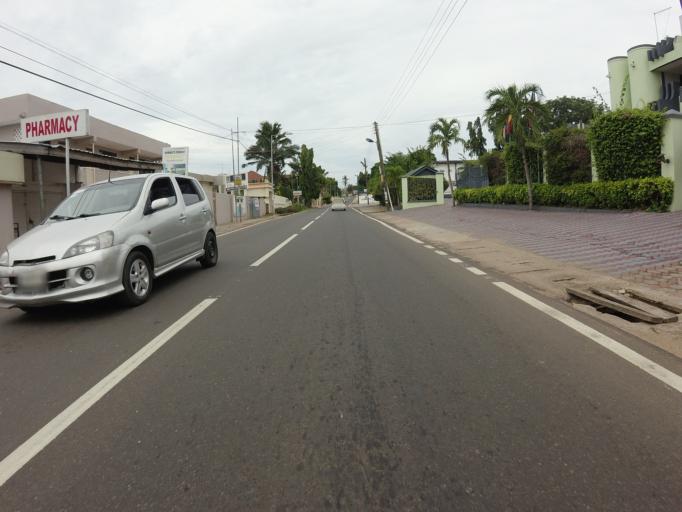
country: GH
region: Greater Accra
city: Dome
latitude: 5.6011
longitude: -0.2309
